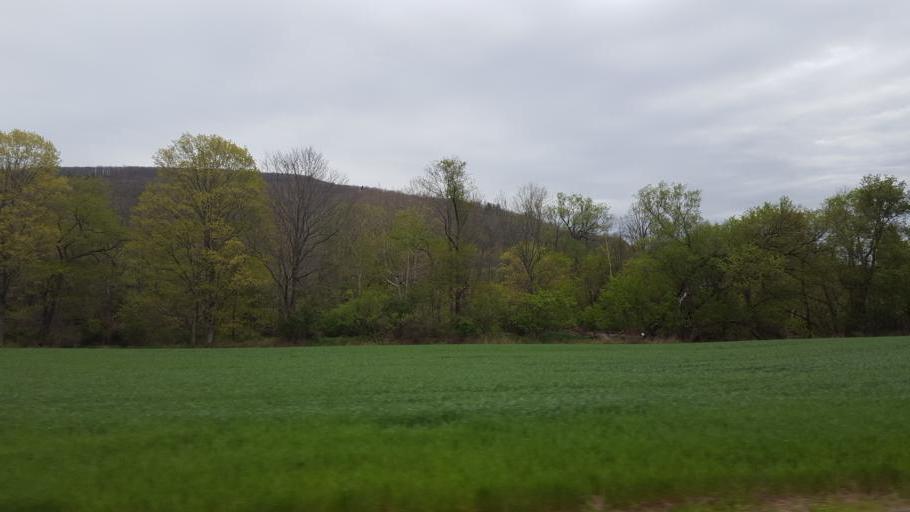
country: US
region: Pennsylvania
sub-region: Tioga County
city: Westfield
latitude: 41.9642
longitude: -77.4461
